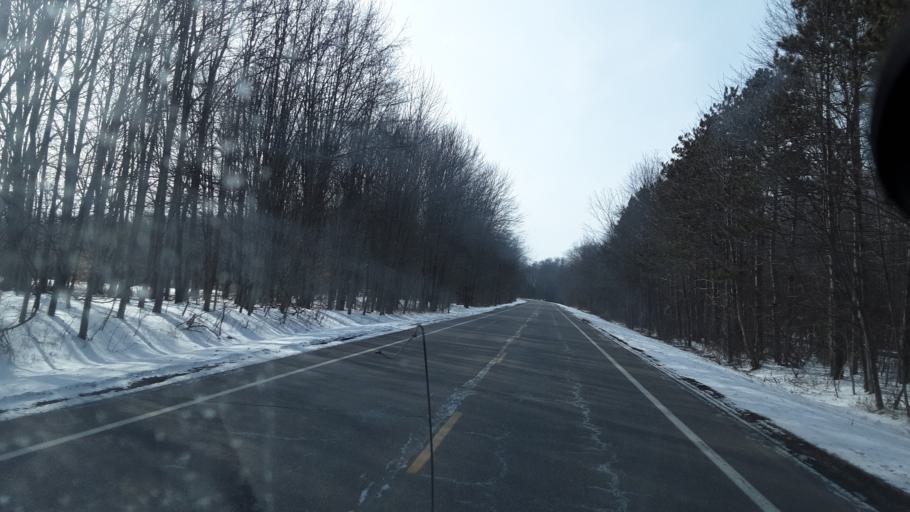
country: US
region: Ohio
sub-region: Portage County
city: Ravenna
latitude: 41.0333
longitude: -81.1974
